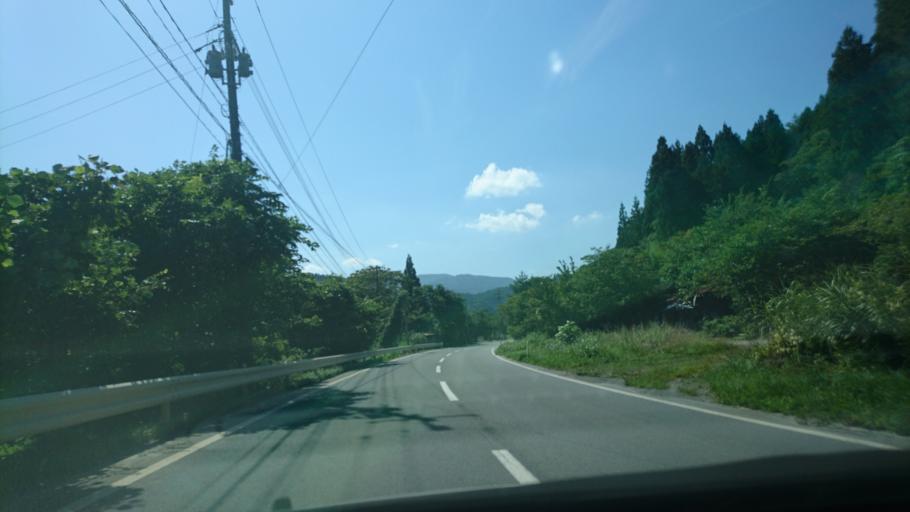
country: JP
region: Iwate
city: Ofunato
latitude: 39.0237
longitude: 141.5665
